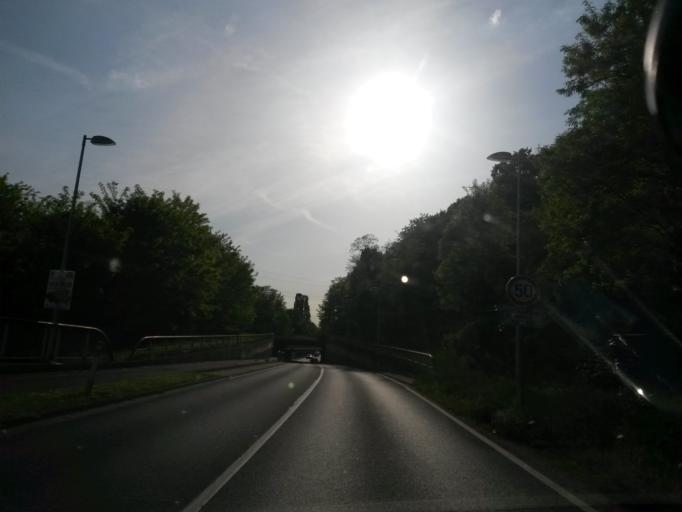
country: DE
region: North Rhine-Westphalia
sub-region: Regierungsbezirk Koln
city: Siegburg
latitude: 50.8019
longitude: 7.1915
